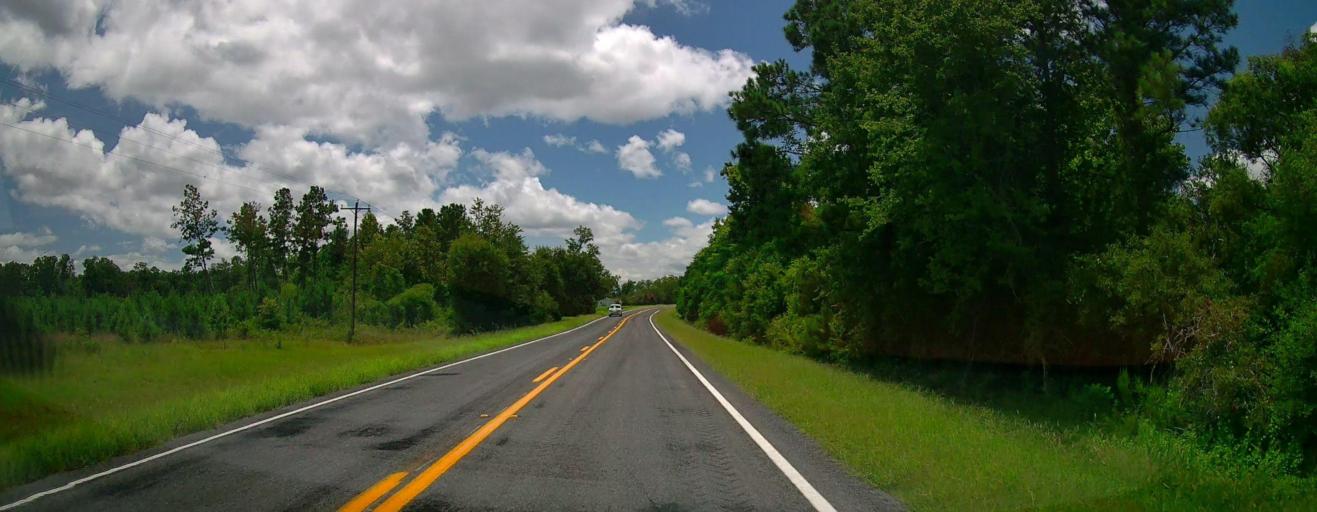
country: US
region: Georgia
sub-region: Turner County
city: Ashburn
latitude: 31.8020
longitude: -83.5776
